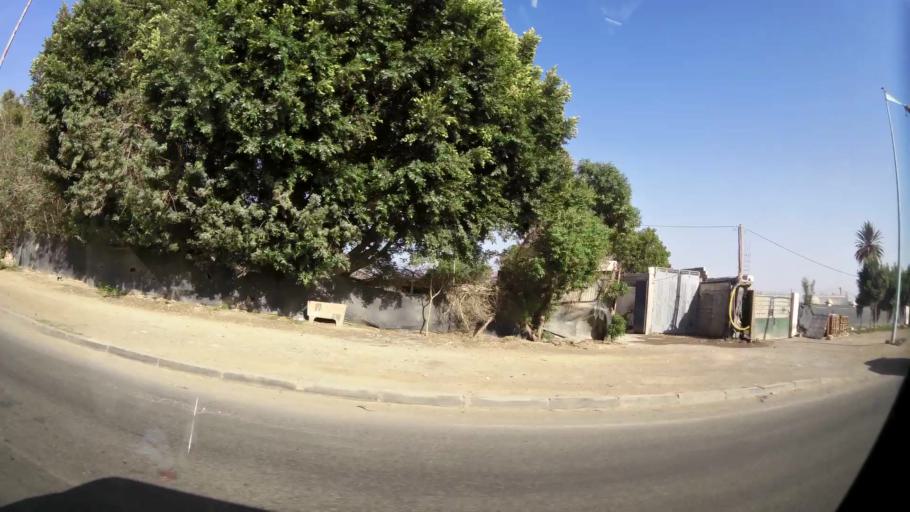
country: MA
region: Souss-Massa-Draa
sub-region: Inezgane-Ait Mellou
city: Inezgane
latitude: 30.3703
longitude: -9.5059
